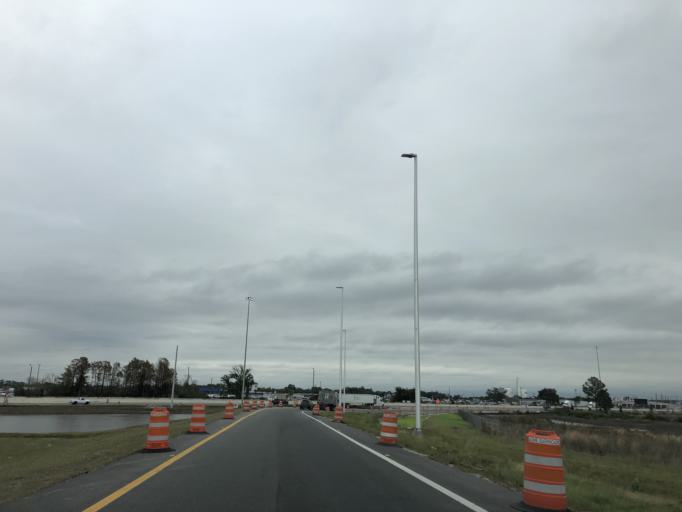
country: US
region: Florida
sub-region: Orange County
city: Sky Lake
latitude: 28.4251
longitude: -81.4001
